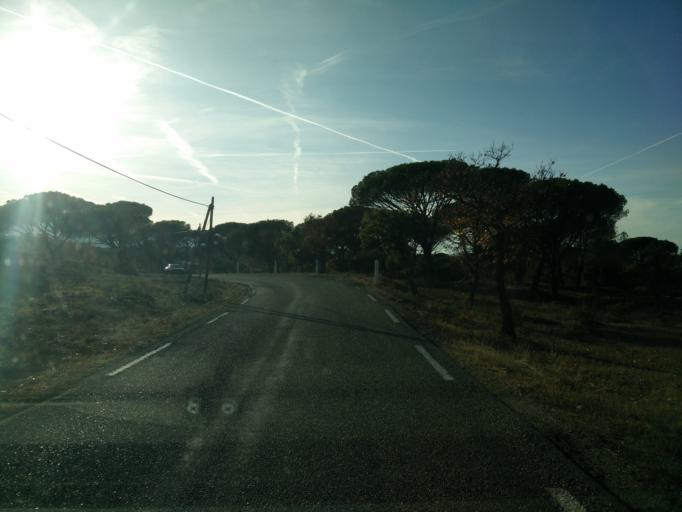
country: FR
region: Provence-Alpes-Cote d'Azur
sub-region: Departement du Var
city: La Garde-Freinet
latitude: 43.3542
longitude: 6.4316
